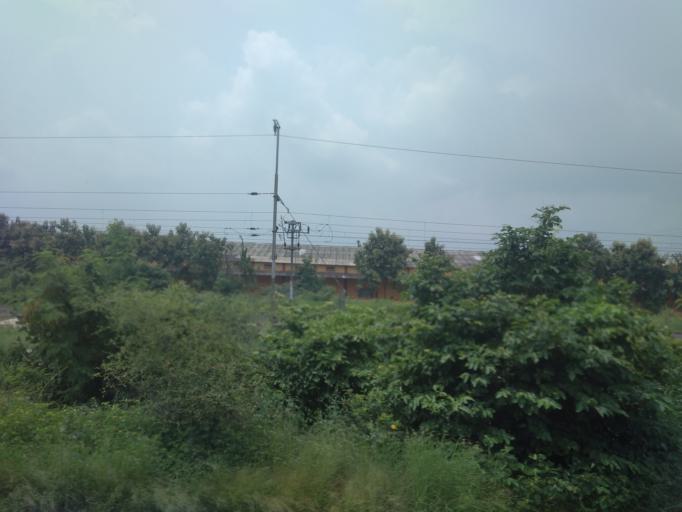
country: IN
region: Telangana
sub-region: Nalgonda
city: Bhongir
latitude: 17.5866
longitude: 78.9896
